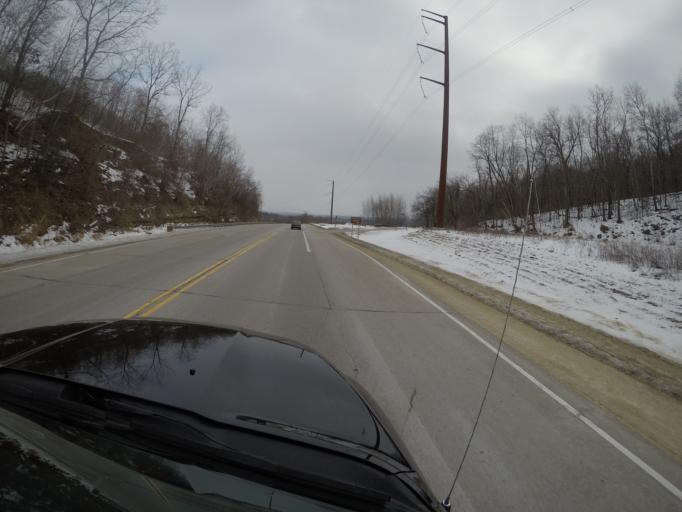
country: US
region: Wisconsin
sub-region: Trempealeau County
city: Galesville
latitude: 44.0715
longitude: -91.3229
